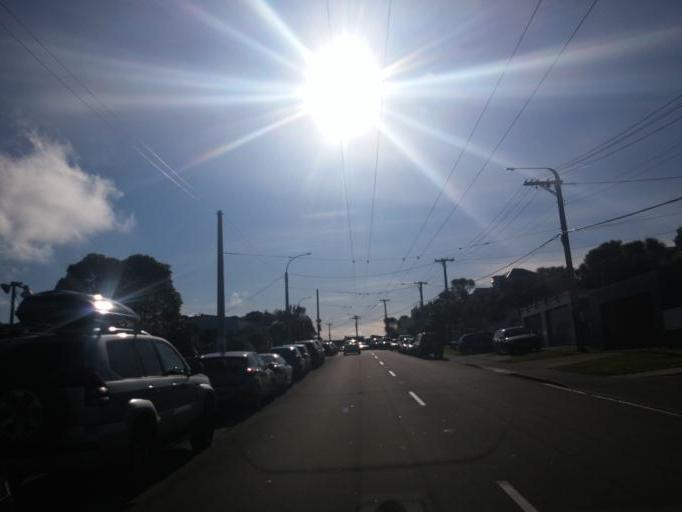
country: NZ
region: Wellington
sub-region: Wellington City
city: Brooklyn
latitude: -41.3168
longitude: 174.7650
